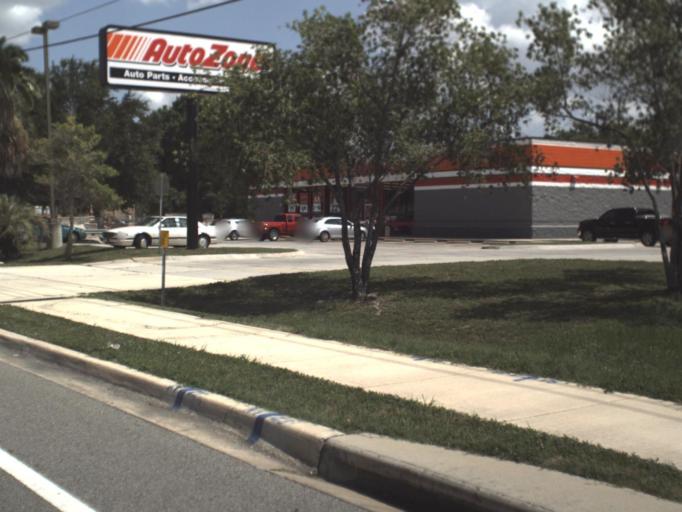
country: US
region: Florida
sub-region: Pinellas County
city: Ridgecrest
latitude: 27.8802
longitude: -82.8218
